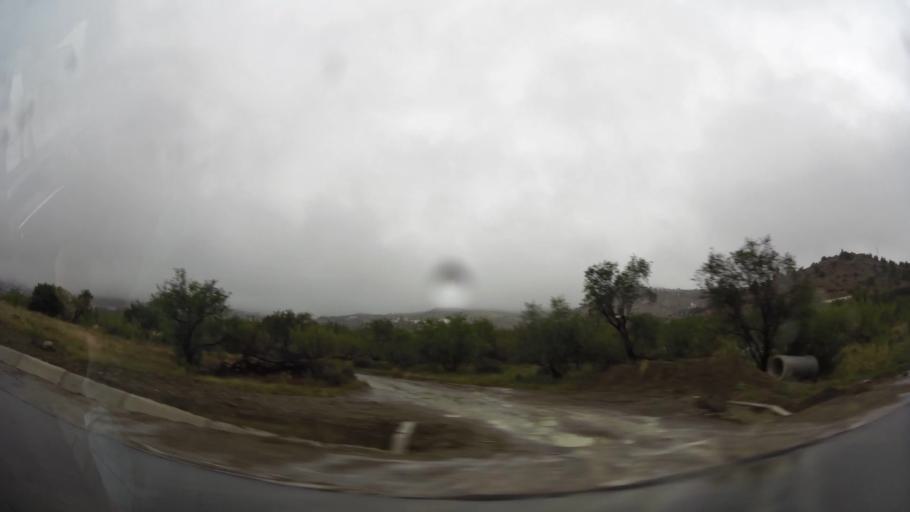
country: MA
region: Oriental
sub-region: Nador
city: Midar
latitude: 34.8250
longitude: -3.7225
